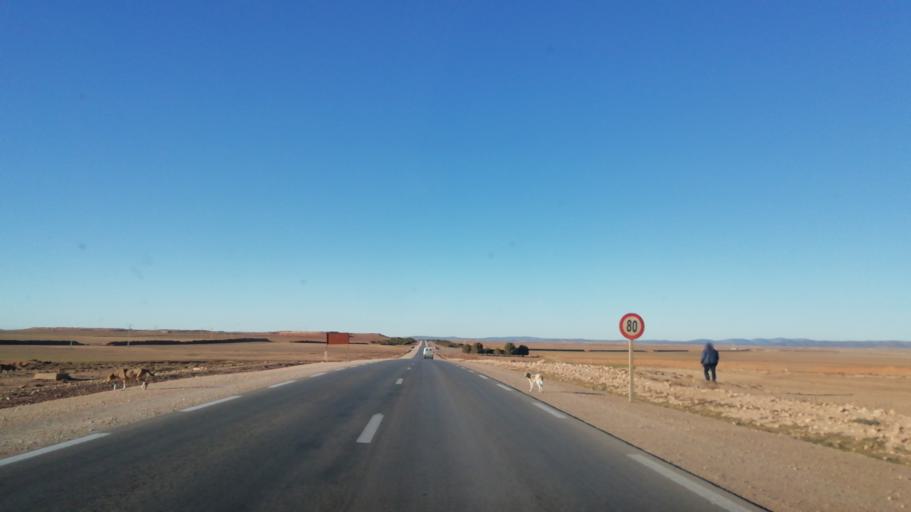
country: DZ
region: Tlemcen
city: Sebdou
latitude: 34.4868
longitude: -1.2728
